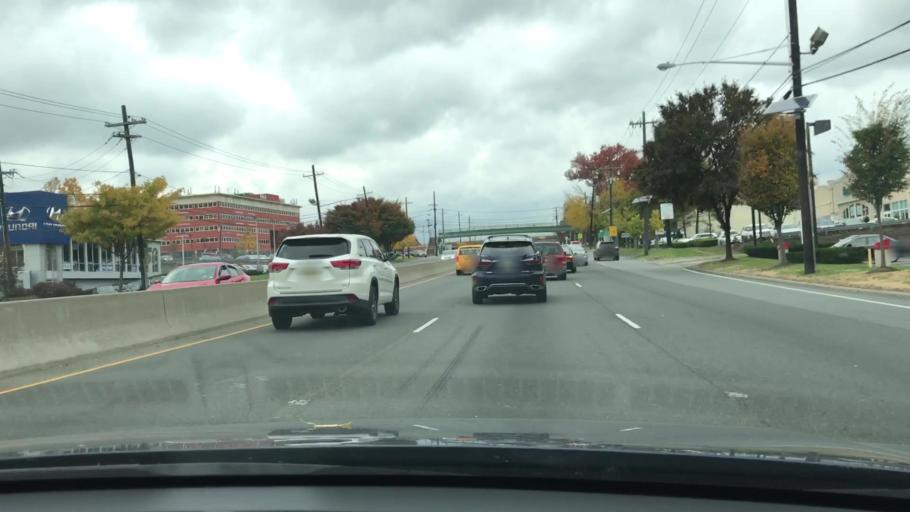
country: US
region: New Jersey
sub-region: Bergen County
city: Maywood
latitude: 40.9152
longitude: -74.0510
